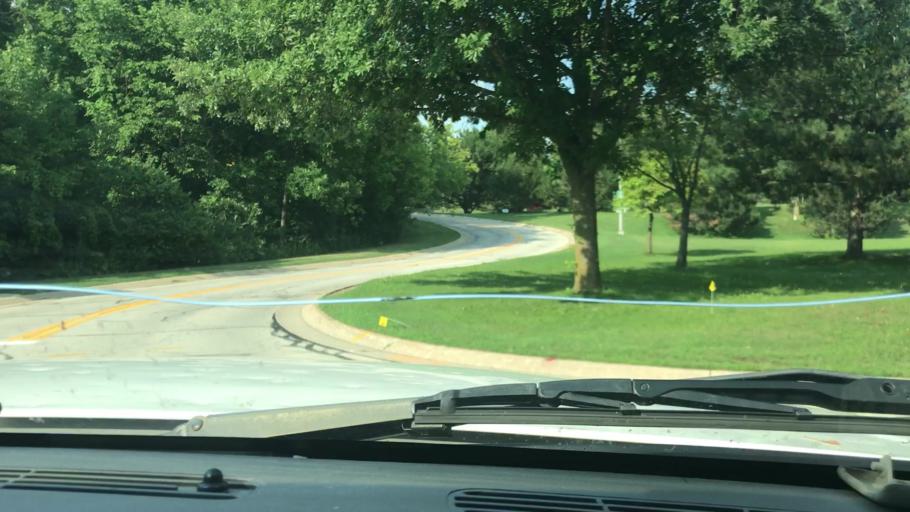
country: US
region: Wisconsin
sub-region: Brown County
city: Bellevue
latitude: 44.5333
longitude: -87.9270
